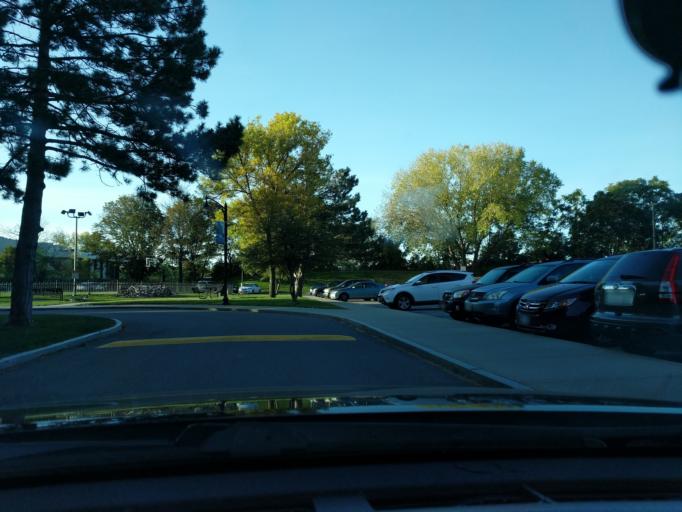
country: US
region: Massachusetts
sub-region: Middlesex County
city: Arlington
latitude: 42.3926
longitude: -71.1387
